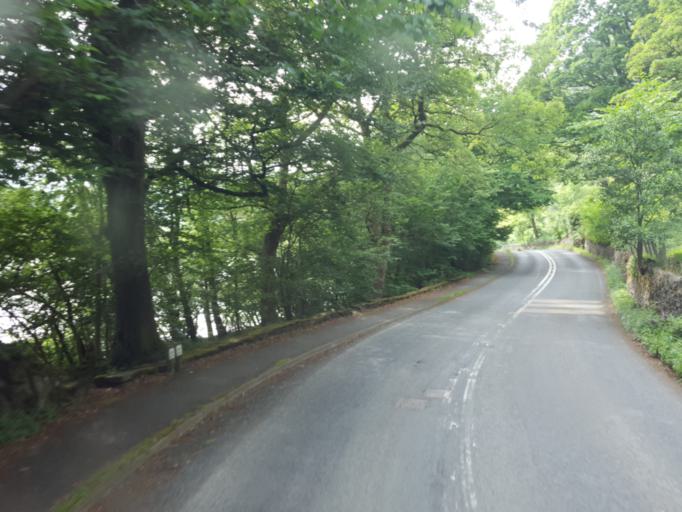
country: GB
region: England
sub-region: Cumbria
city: Ambleside
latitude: 54.4480
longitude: -2.9872
